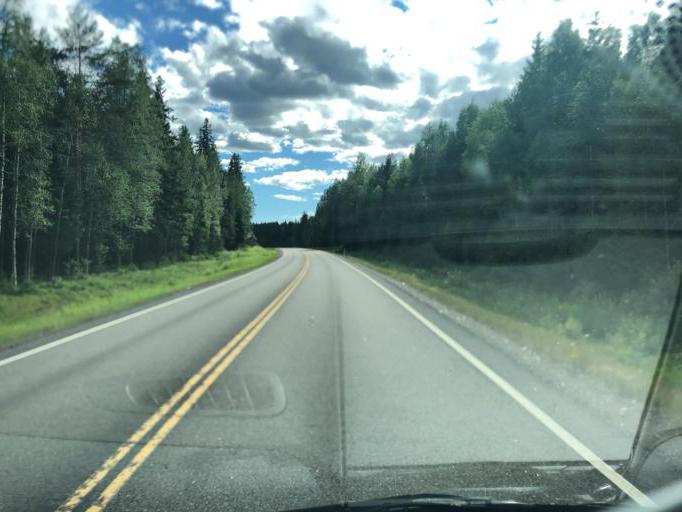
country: FI
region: Kymenlaakso
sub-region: Kouvola
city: Kouvola
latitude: 60.9981
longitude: 26.9290
